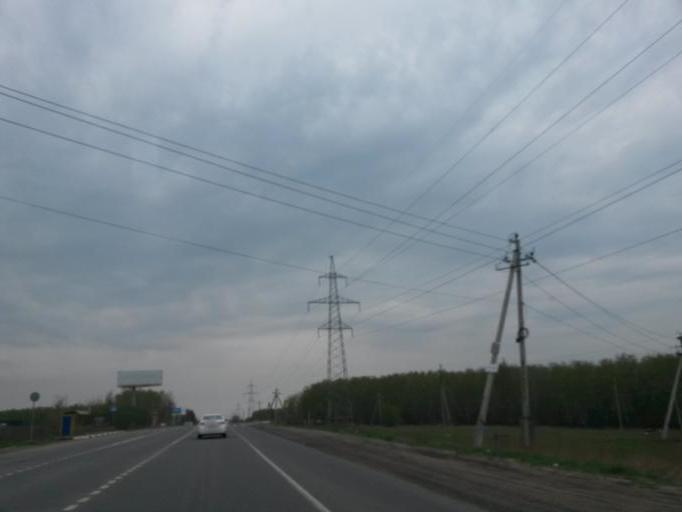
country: RU
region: Moskovskaya
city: Shcherbinka
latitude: 55.4875
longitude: 37.5995
